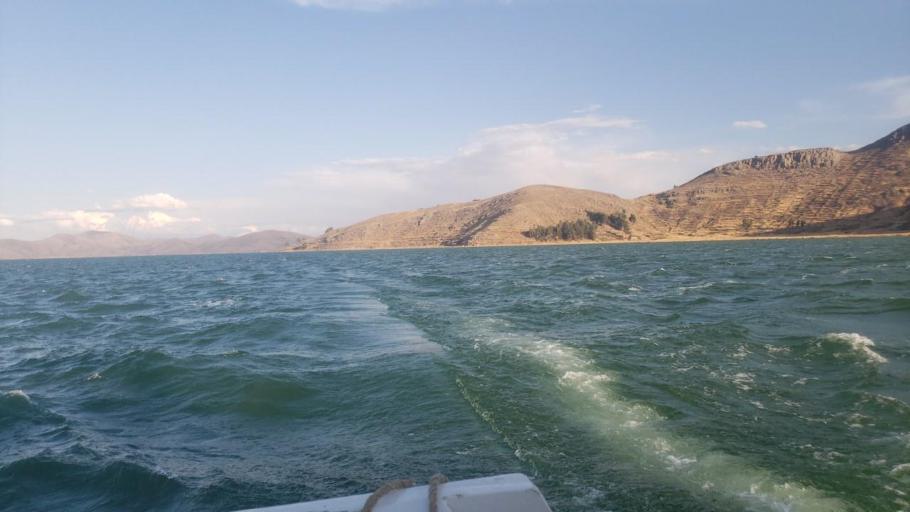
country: BO
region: La Paz
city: San Pablo
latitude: -16.2895
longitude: -68.7646
